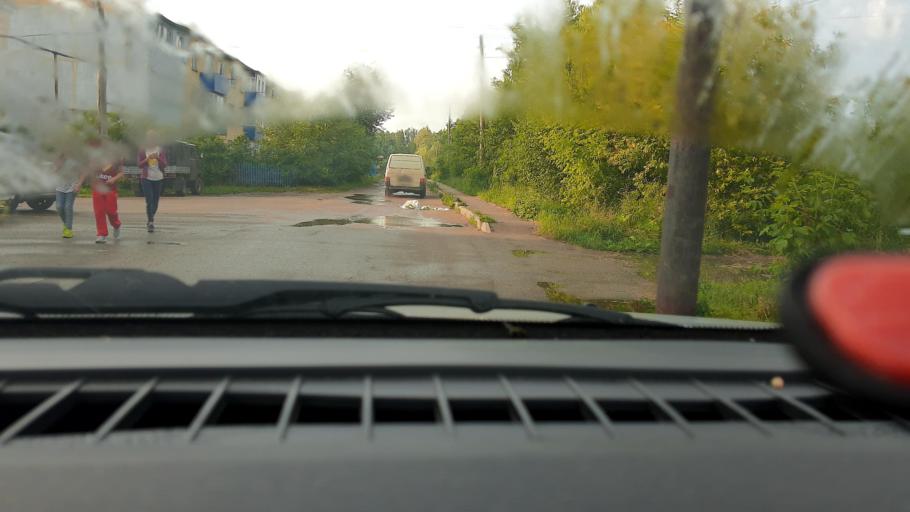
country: RU
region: Nizjnij Novgorod
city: Lukoyanov
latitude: 55.0438
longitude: 44.4944
